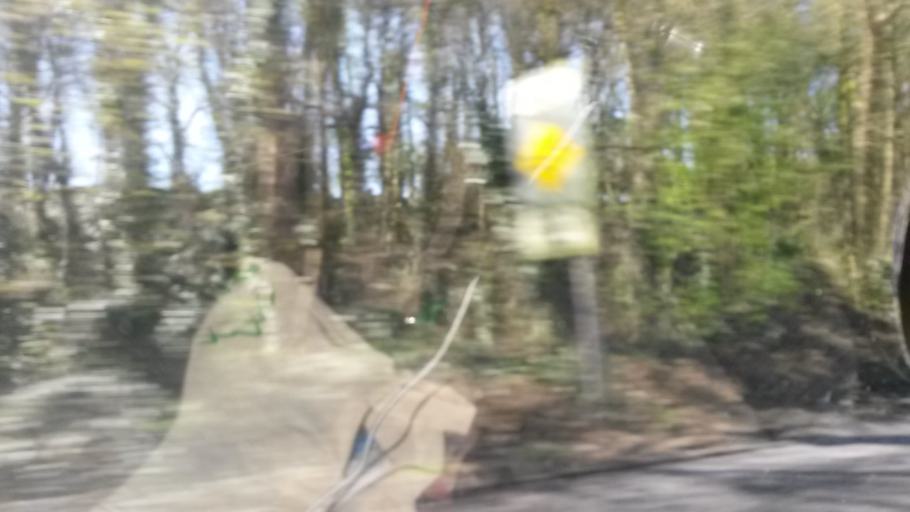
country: IE
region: Munster
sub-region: County Cork
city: Blarney
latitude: 51.8971
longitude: -8.5558
